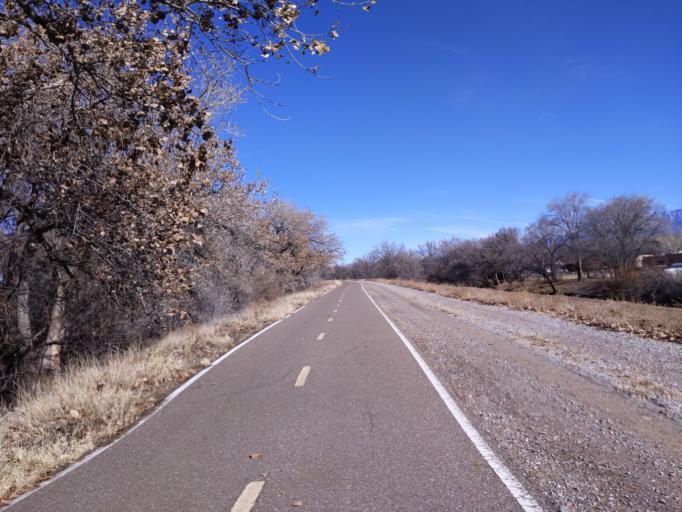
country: US
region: New Mexico
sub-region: Bernalillo County
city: Lee Acres
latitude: 35.1473
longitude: -106.6730
